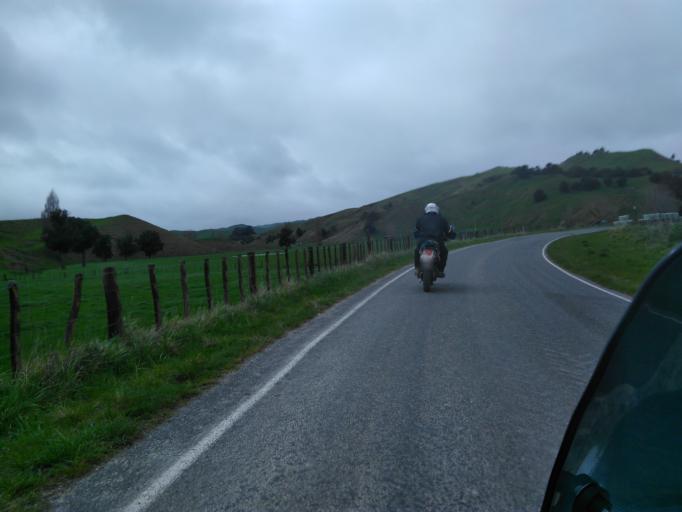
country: NZ
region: Gisborne
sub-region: Gisborne District
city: Gisborne
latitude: -38.6349
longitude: 177.6928
